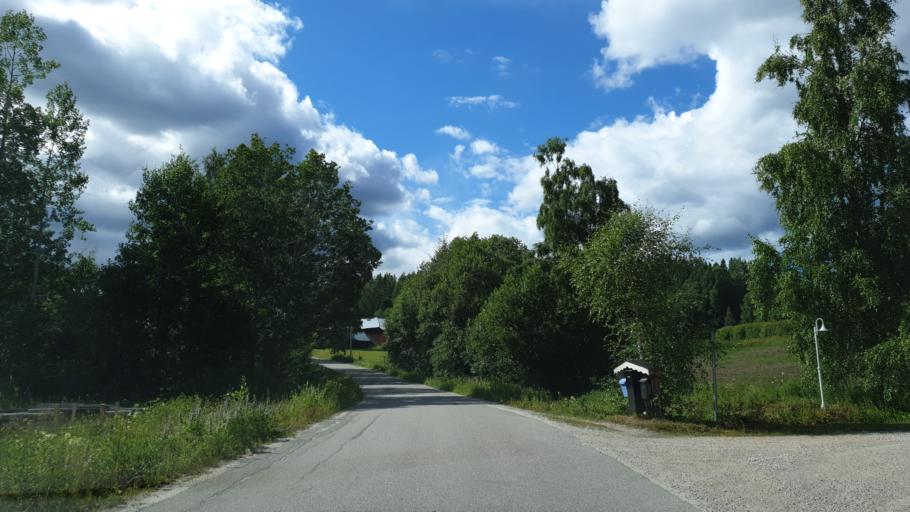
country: SE
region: Gaevleborg
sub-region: Nordanstigs Kommun
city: Bergsjoe
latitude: 62.0408
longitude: 17.0920
